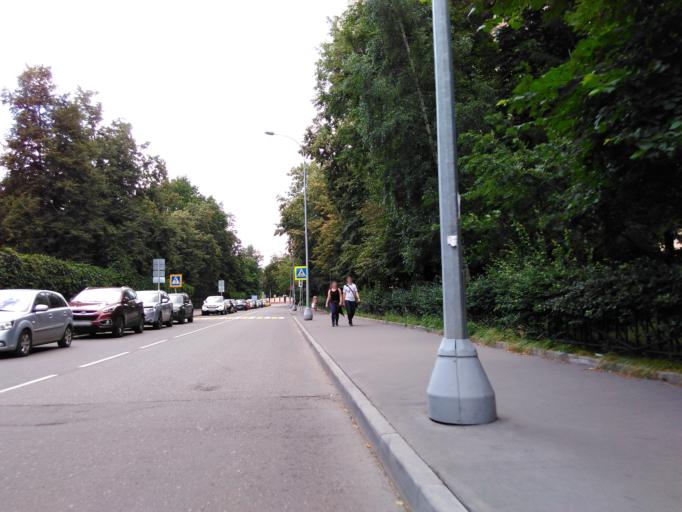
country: RU
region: Moskovskaya
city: Dorogomilovo
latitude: 55.7299
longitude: 37.5793
